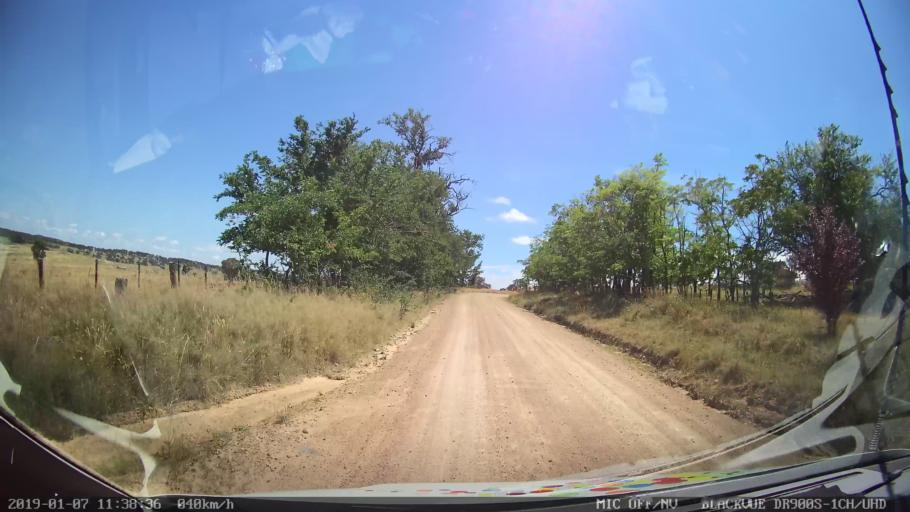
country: AU
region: New South Wales
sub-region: Armidale Dumaresq
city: Armidale
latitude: -30.3705
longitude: 151.5726
